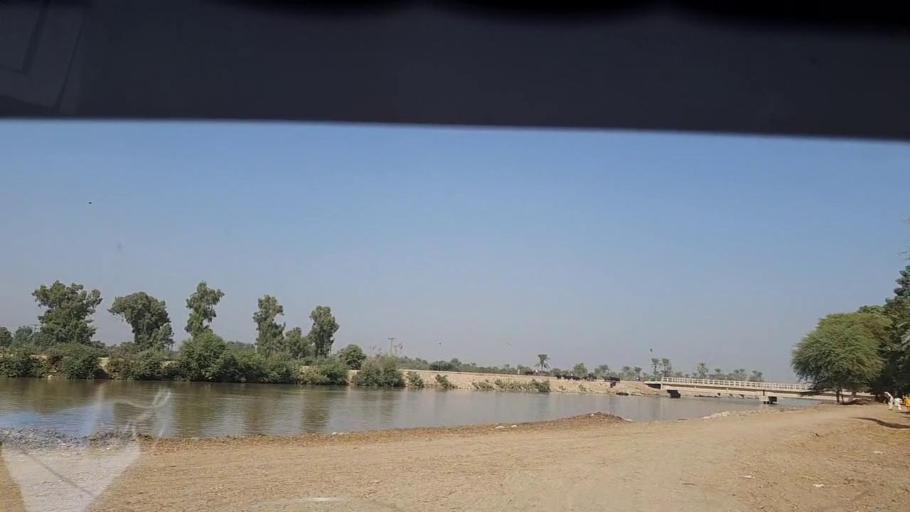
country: PK
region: Sindh
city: Naudero
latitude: 27.6632
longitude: 68.3741
